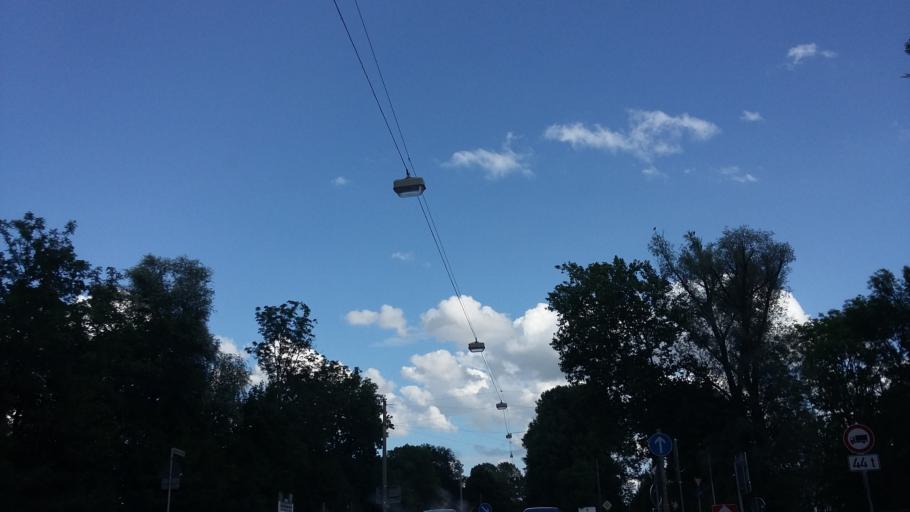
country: DE
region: Bavaria
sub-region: Swabia
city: Augsburg
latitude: 48.3813
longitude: 10.9038
